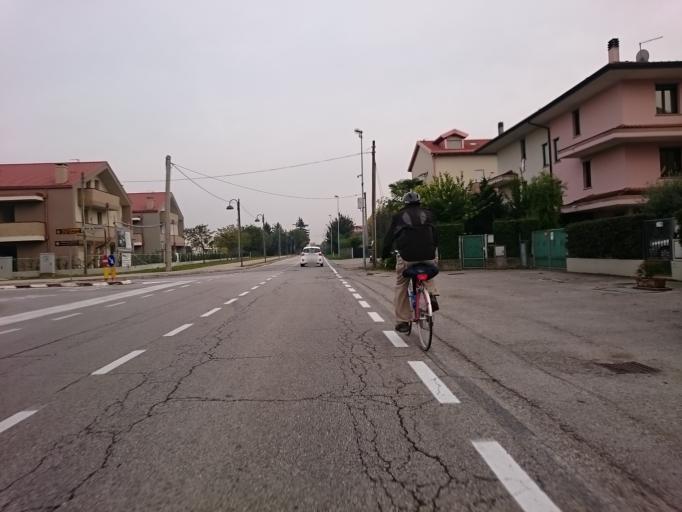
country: IT
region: Veneto
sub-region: Provincia di Padova
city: Mandriola-Sant'Agostino
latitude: 45.3618
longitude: 11.8469
